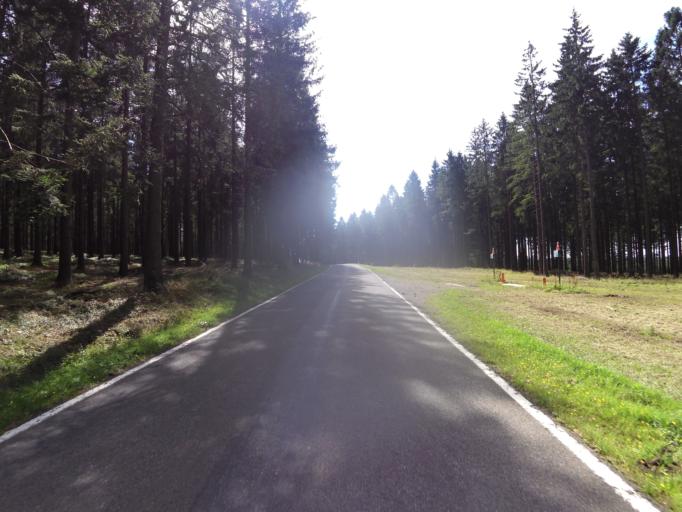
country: BE
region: Wallonia
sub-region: Province du Luxembourg
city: Saint-Hubert
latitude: 50.0543
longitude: 5.3463
